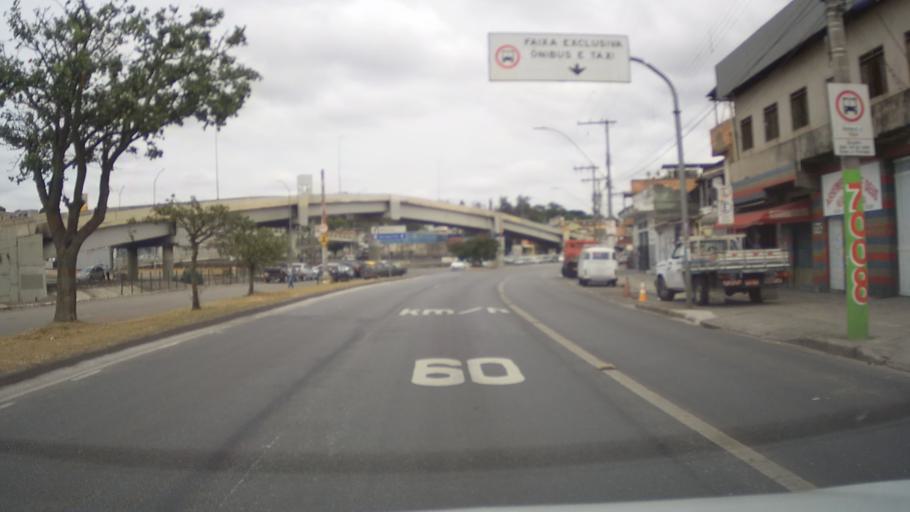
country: BR
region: Minas Gerais
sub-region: Belo Horizonte
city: Belo Horizonte
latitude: -19.8638
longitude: -43.9299
